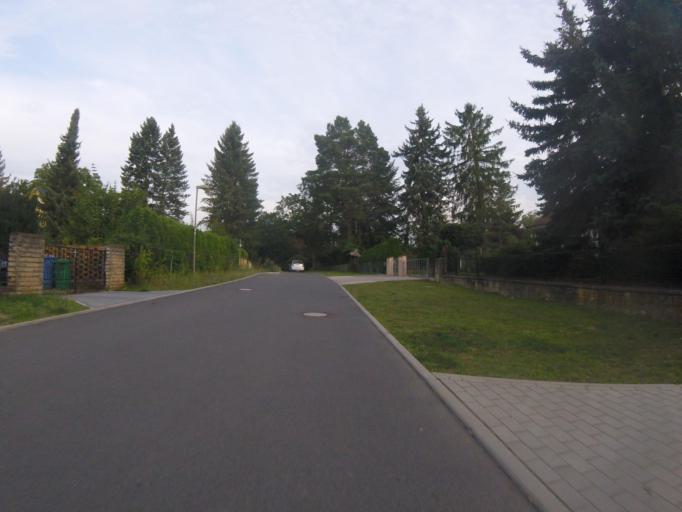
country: DE
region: Brandenburg
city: Wildau
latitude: 52.3363
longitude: 13.6129
